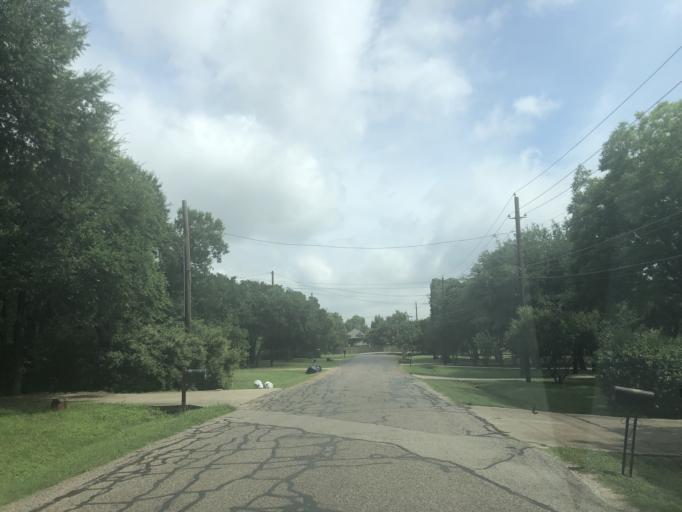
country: US
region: Texas
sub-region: Dallas County
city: Irving
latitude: 32.8002
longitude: -96.9671
